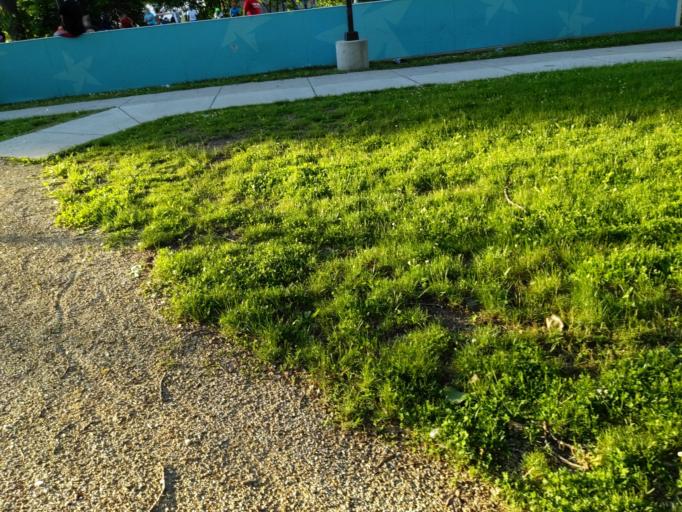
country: US
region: Michigan
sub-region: Ingham County
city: Lansing
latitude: 42.6965
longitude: -84.5805
